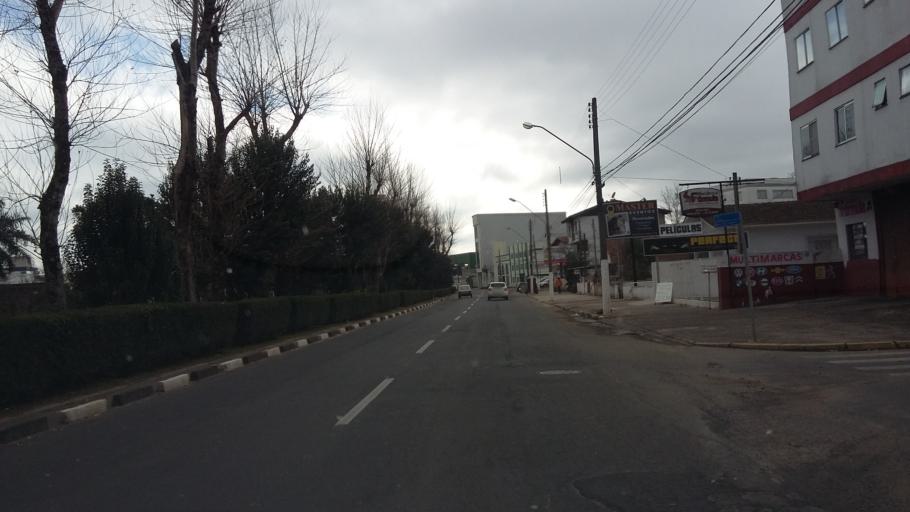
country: BR
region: Santa Catarina
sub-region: Lages
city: Lages
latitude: -27.8149
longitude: -50.3177
